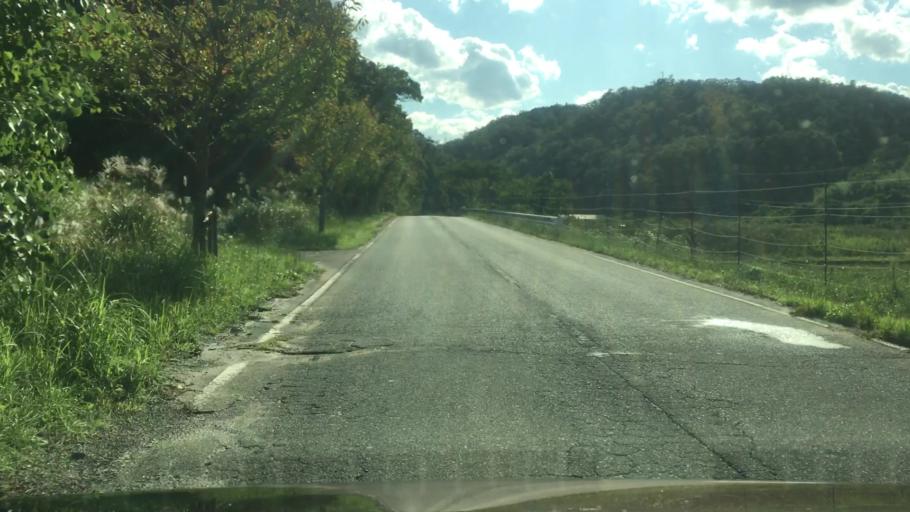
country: JP
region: Hyogo
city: Toyooka
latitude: 35.6462
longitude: 134.9637
